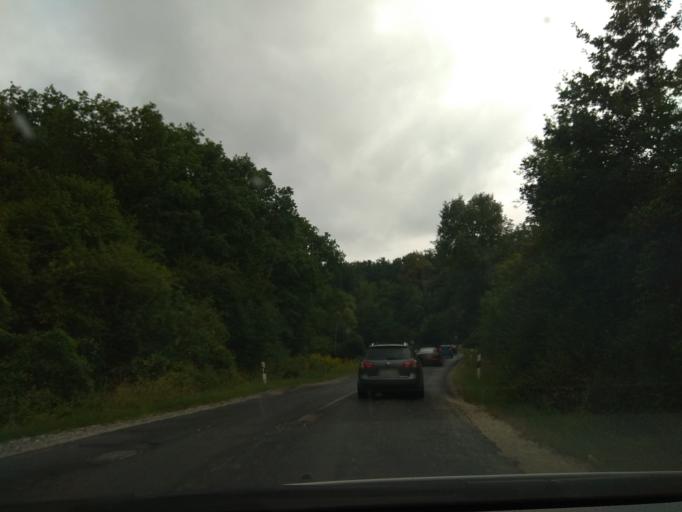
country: HU
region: Borsod-Abauj-Zemplen
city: Harsany
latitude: 48.0133
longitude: 20.7638
